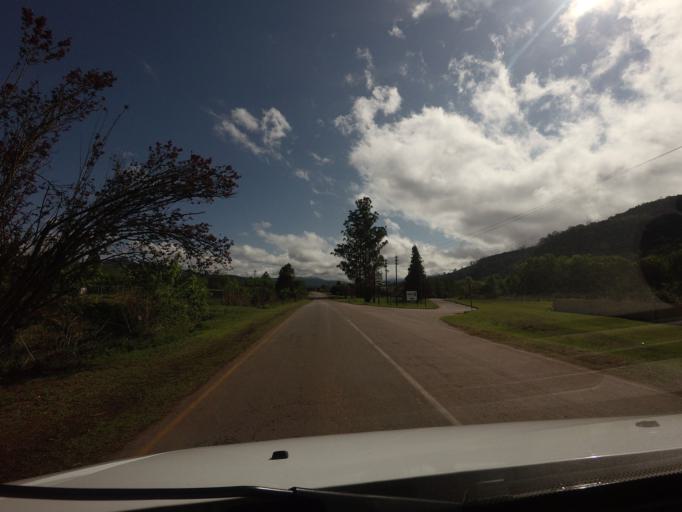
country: ZA
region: Mpumalanga
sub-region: Ehlanzeni District
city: Graksop
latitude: -25.0932
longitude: 30.7726
